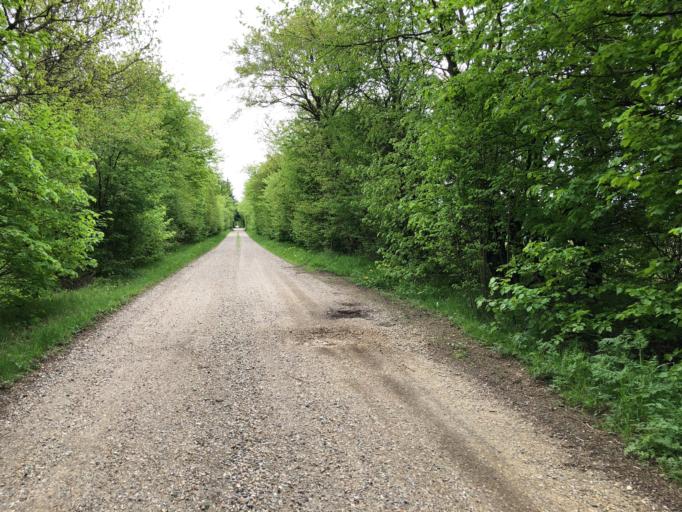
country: DK
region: Central Jutland
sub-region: Holstebro Kommune
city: Ulfborg
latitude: 56.2680
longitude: 8.4259
